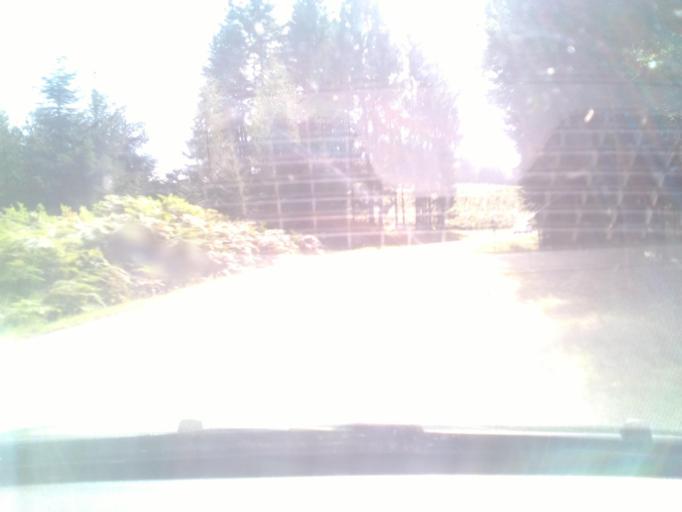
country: FR
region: Lorraine
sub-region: Departement des Vosges
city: Bruyeres
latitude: 48.2846
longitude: 6.7854
